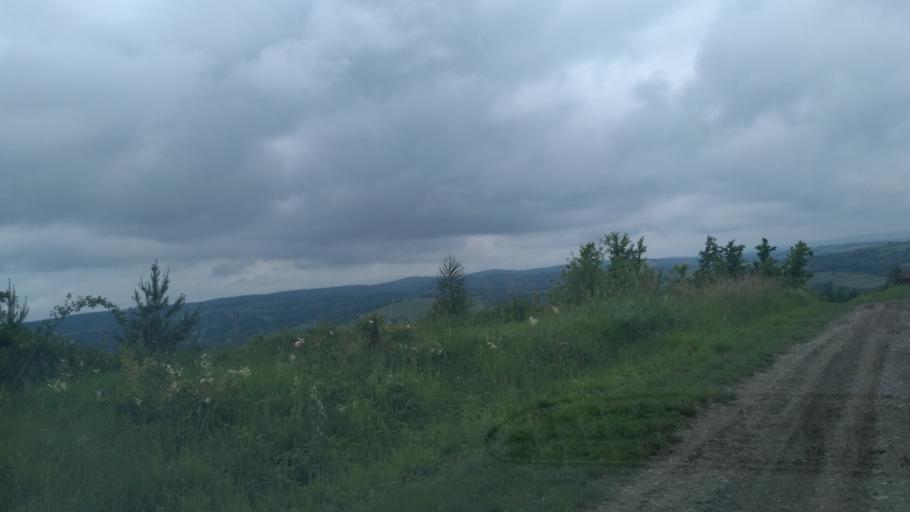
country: PL
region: Subcarpathian Voivodeship
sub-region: Powiat jaroslawski
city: Pruchnik
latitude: 49.8880
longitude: 22.5138
